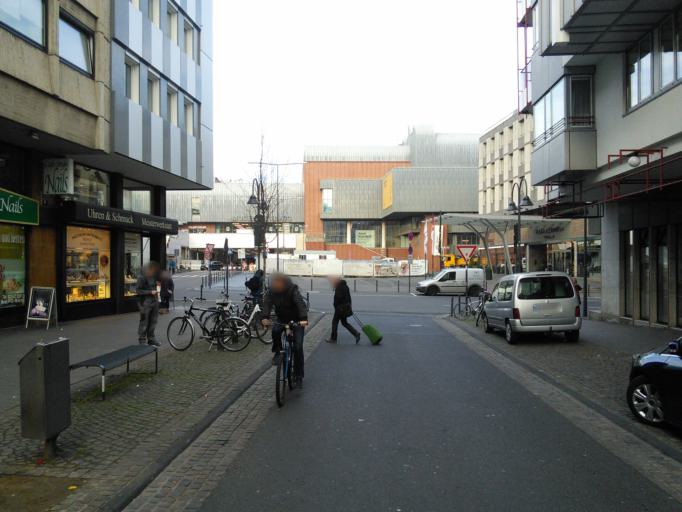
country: DE
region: North Rhine-Westphalia
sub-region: Regierungsbezirk Koln
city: Altstadt Nord
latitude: 50.9395
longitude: 6.9601
